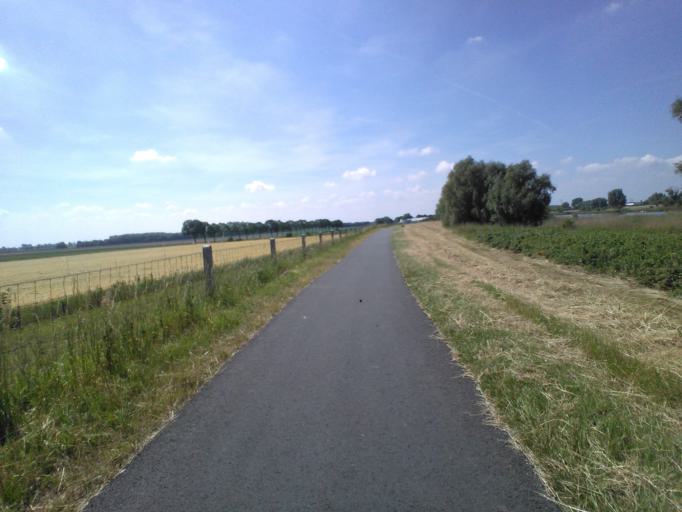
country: NL
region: North Brabant
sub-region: Gemeente Werkendam
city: Werkendam
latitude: 51.7886
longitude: 4.8774
